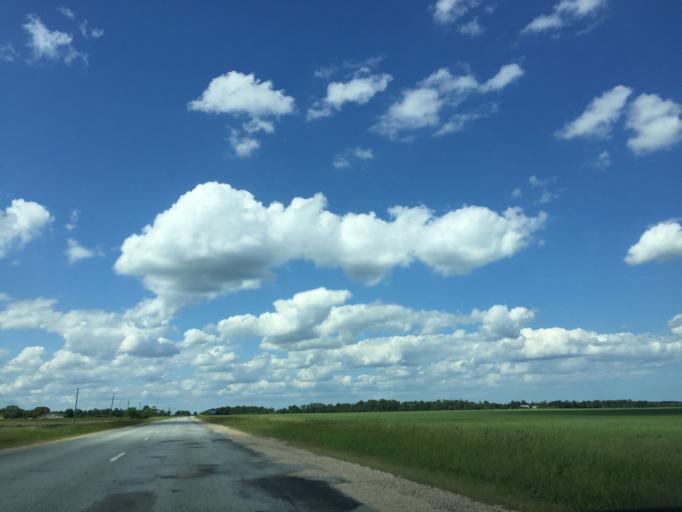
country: LV
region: Engure
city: Smarde
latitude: 56.8027
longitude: 23.3630
